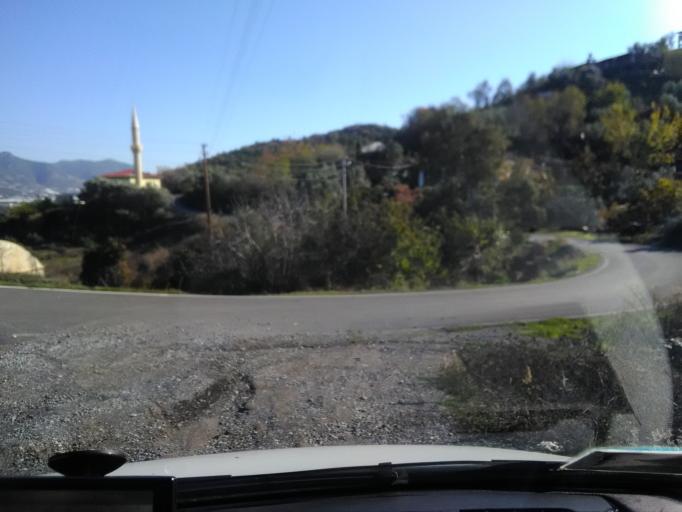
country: TR
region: Antalya
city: Gazipasa
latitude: 36.2479
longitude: 32.3356
